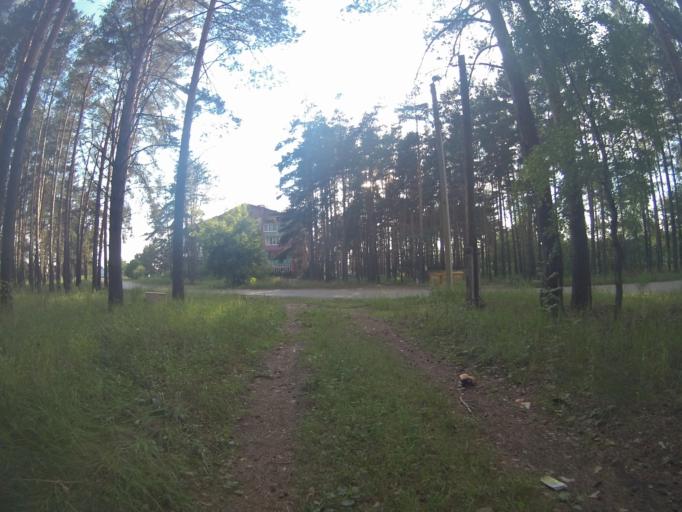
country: RU
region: Vladimir
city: Kommunar
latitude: 56.1196
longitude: 40.4597
